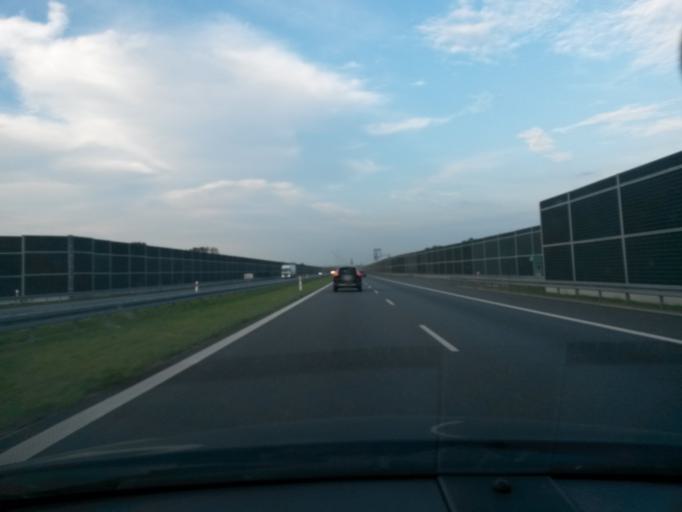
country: PL
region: Masovian Voivodeship
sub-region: Powiat zyrardowski
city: Zyrardow
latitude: 52.1062
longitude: 20.4457
